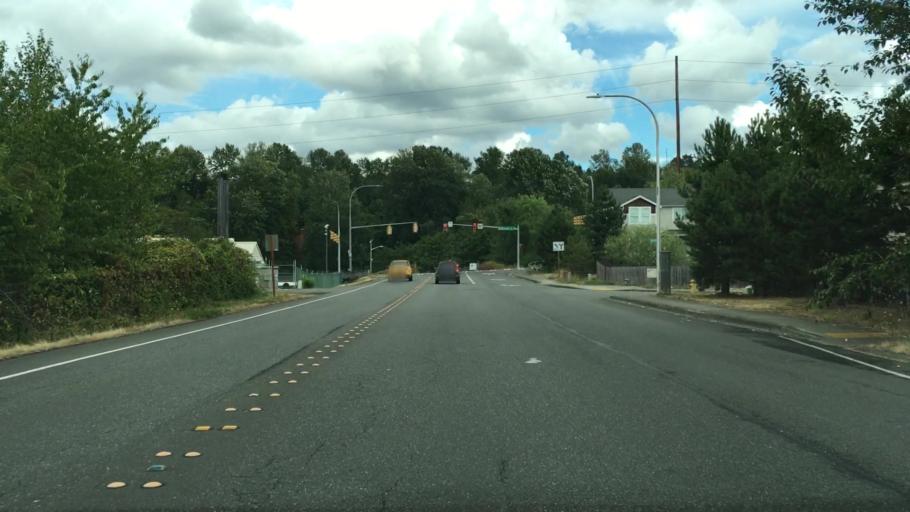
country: US
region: Washington
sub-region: King County
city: Renton
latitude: 47.4610
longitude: -122.2087
